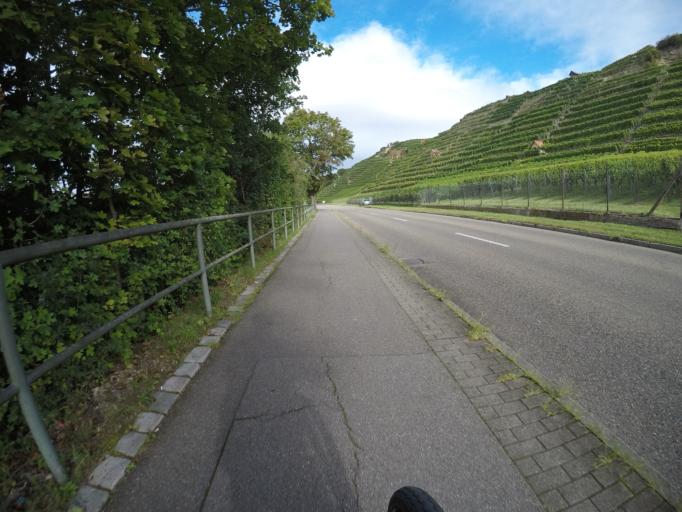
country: DE
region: Baden-Wuerttemberg
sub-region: Regierungsbezirk Stuttgart
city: Stuttgart Muehlhausen
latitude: 48.8237
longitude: 9.2255
